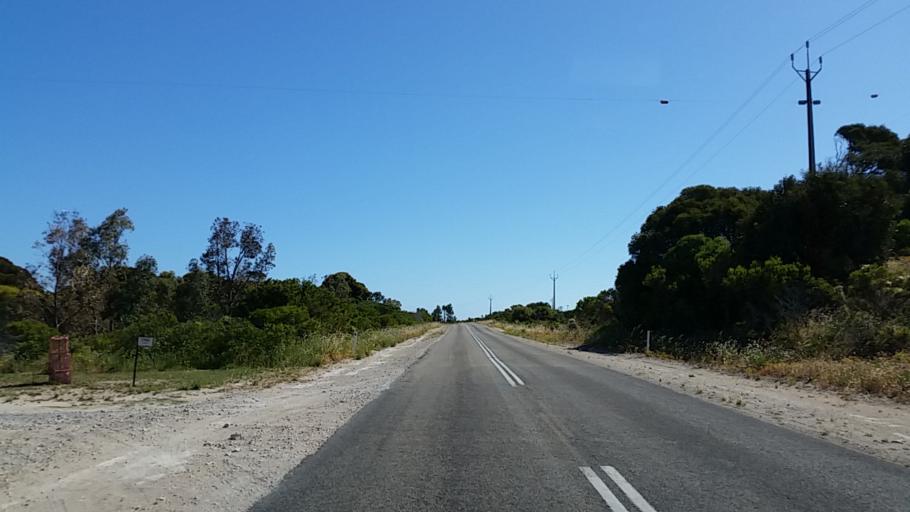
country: AU
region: South Australia
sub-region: Yorke Peninsula
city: Honiton
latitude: -35.2269
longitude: 136.9873
